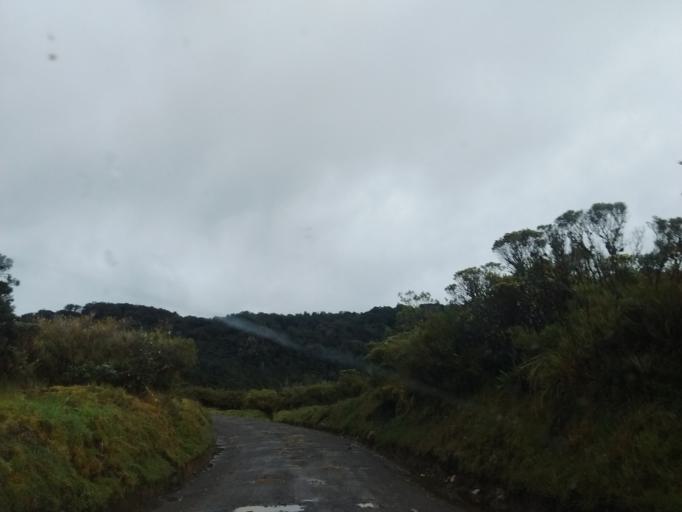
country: CO
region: Cauca
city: Totoro
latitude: 2.3539
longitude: -76.3376
